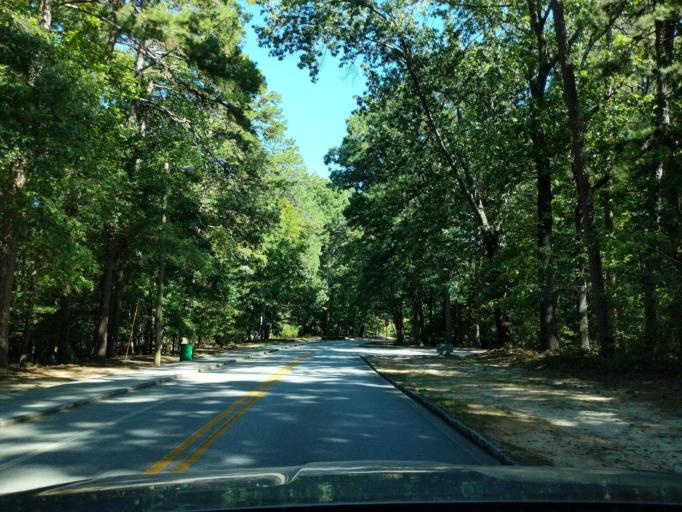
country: US
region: Georgia
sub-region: DeKalb County
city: Stone Mountain
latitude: 33.8055
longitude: -84.1609
